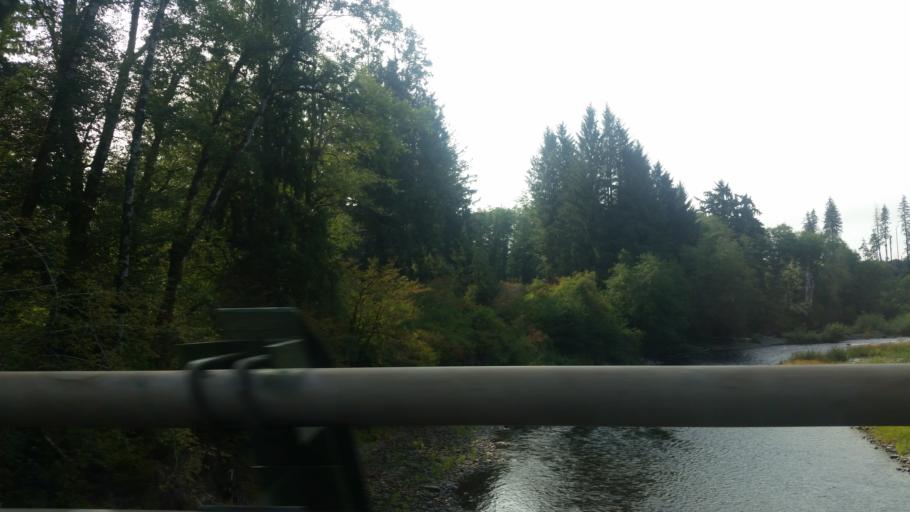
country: US
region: Washington
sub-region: Clallam County
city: Forks
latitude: 47.9839
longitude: -124.3981
